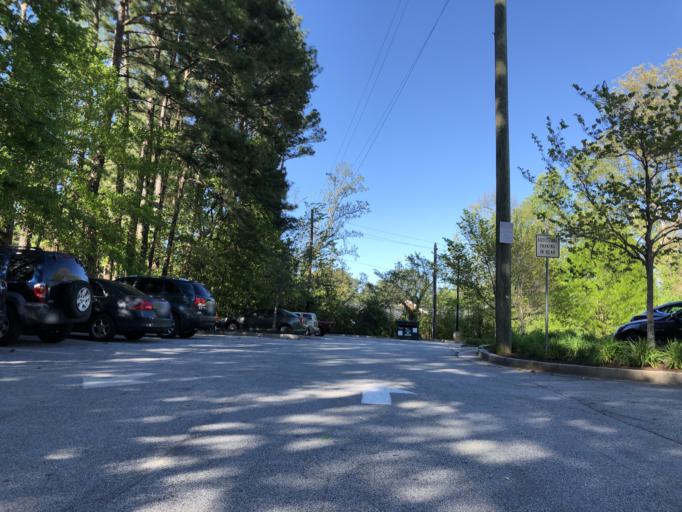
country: US
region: Georgia
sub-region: DeKalb County
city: North Druid Hills
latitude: 33.8095
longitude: -84.3077
